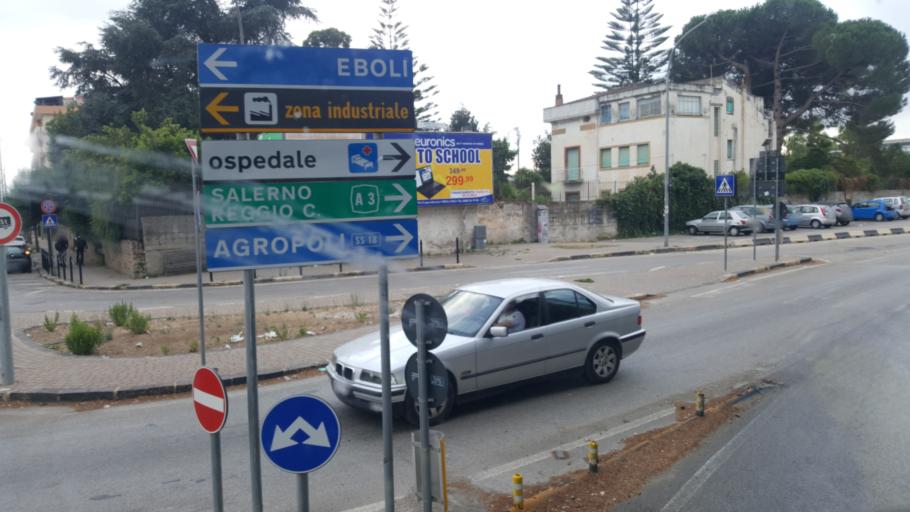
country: IT
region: Campania
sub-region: Provincia di Salerno
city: Battipaglia
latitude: 40.6029
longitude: 14.9818
